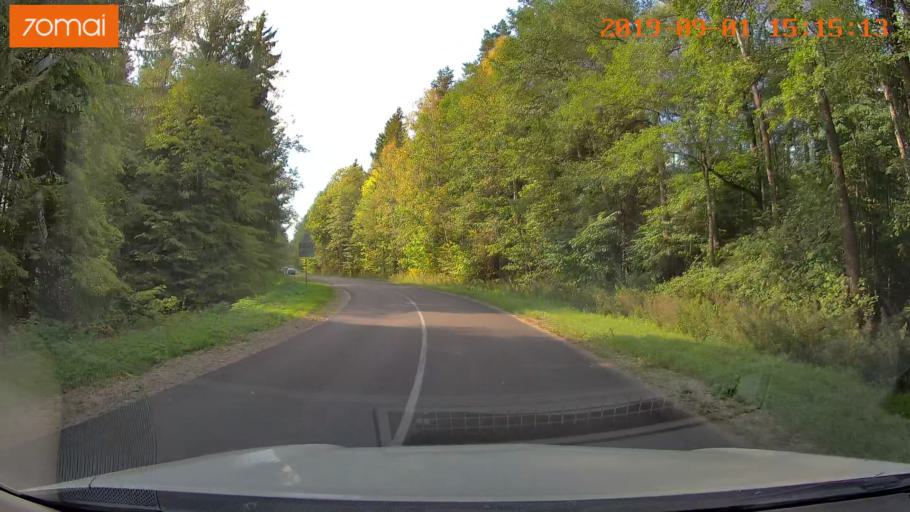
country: RU
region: Kaluga
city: Maloyaroslavets
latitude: 54.8782
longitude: 36.5422
